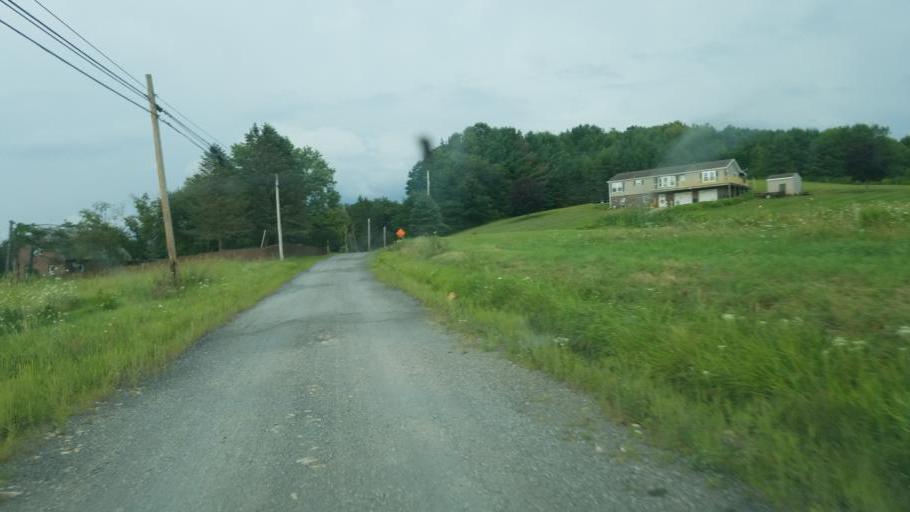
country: US
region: Pennsylvania
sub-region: Clarion County
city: Knox
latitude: 41.2551
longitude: -79.5529
